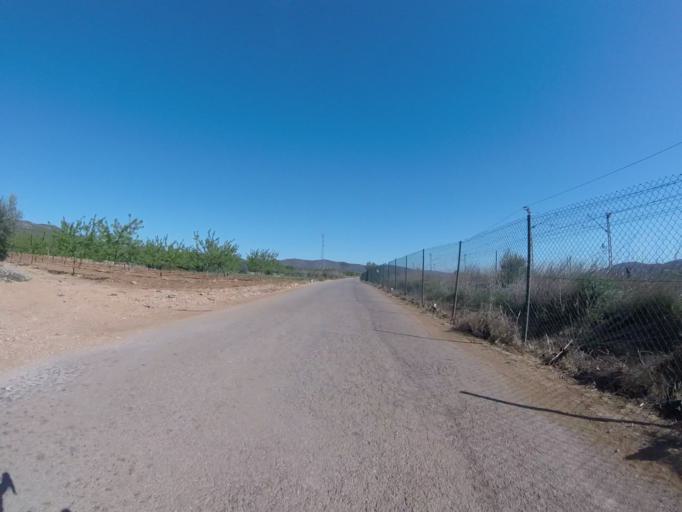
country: ES
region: Valencia
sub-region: Provincia de Castello
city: Alcala de Xivert
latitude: 40.3173
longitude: 0.2337
